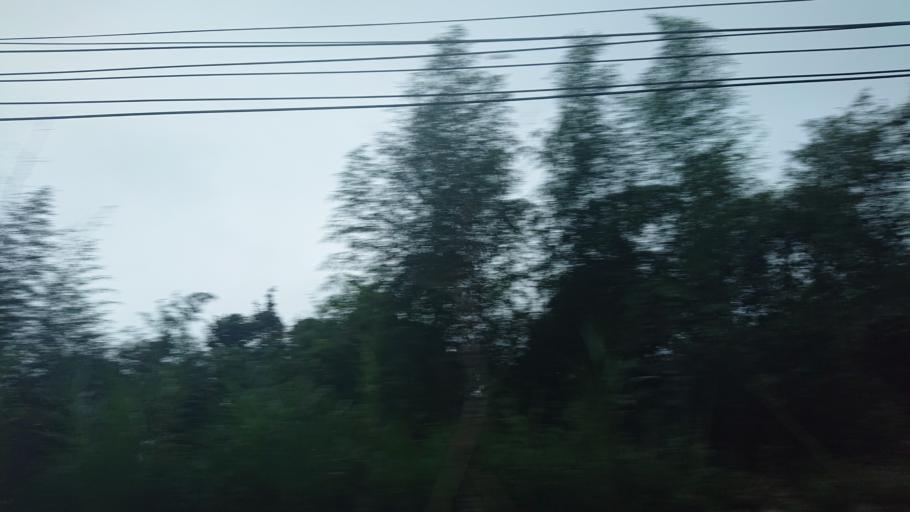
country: TW
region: Taiwan
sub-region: Chiayi
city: Jiayi Shi
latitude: 23.4719
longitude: 120.7182
